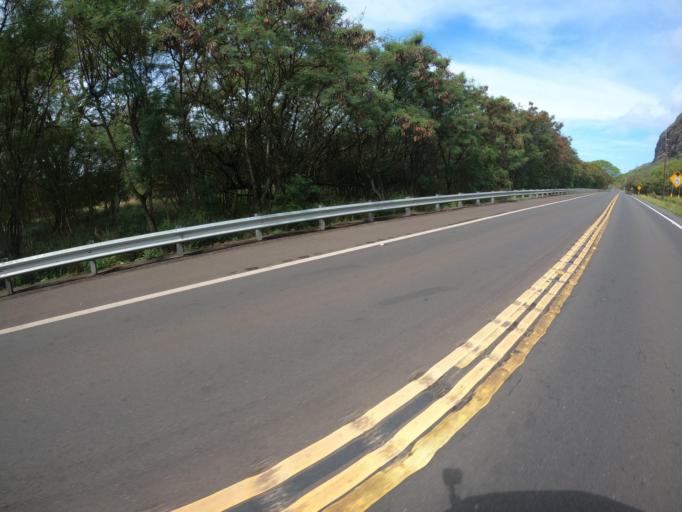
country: US
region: Hawaii
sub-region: Honolulu County
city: Makaha Valley
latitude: 21.5366
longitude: -158.2284
